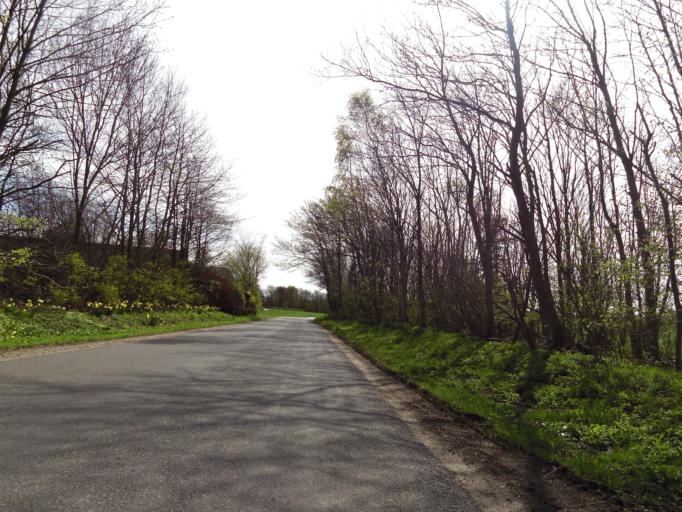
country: DK
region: Central Jutland
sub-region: Skive Kommune
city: Skive
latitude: 56.5439
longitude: 8.9551
